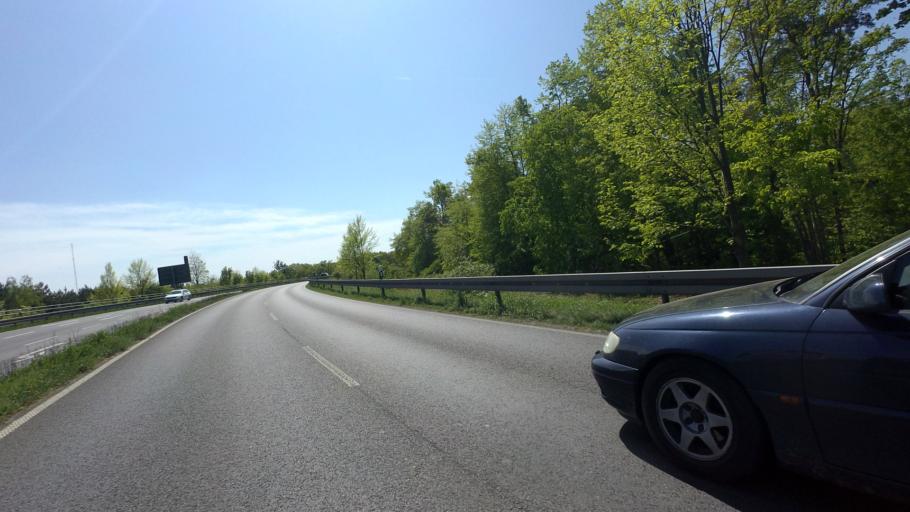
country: DE
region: Brandenburg
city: Wildau
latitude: 52.3143
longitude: 13.6020
